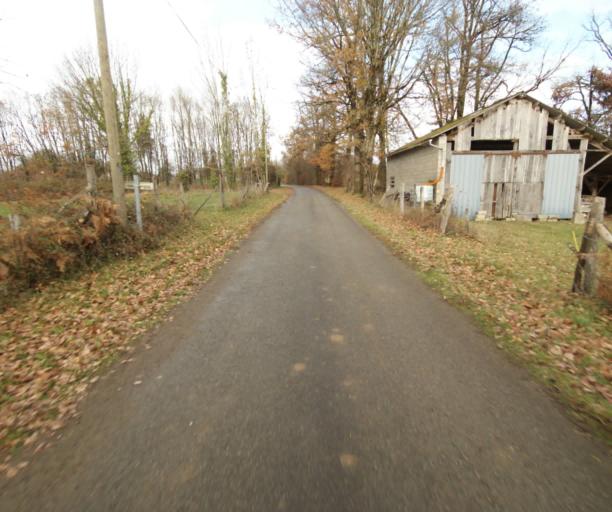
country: FR
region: Limousin
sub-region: Departement de la Correze
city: Sainte-Fereole
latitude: 45.2657
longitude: 1.6022
